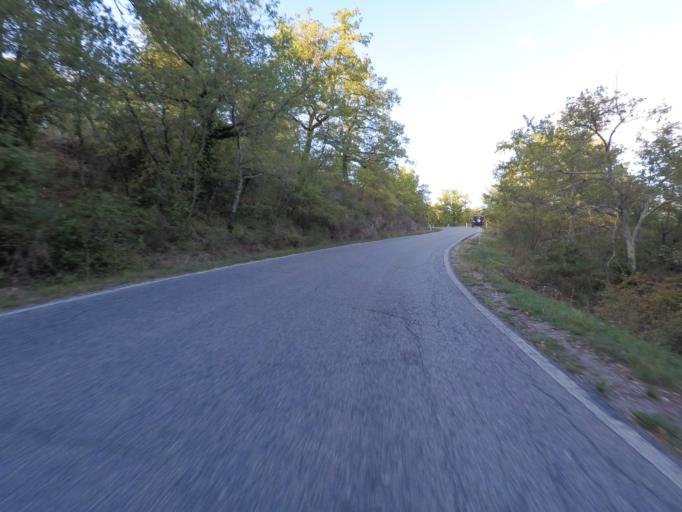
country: IT
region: Tuscany
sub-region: Provincia di Siena
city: Radda in Chianti
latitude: 43.4770
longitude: 11.3718
